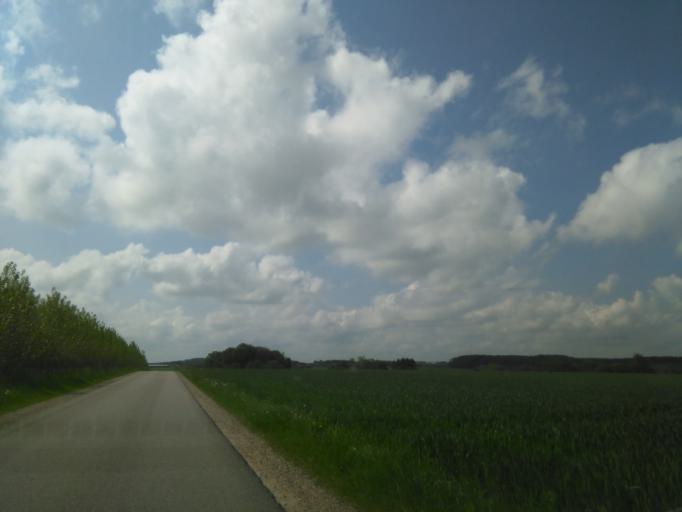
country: DK
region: Central Jutland
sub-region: Arhus Kommune
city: Sabro
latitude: 56.2155
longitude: 9.9772
